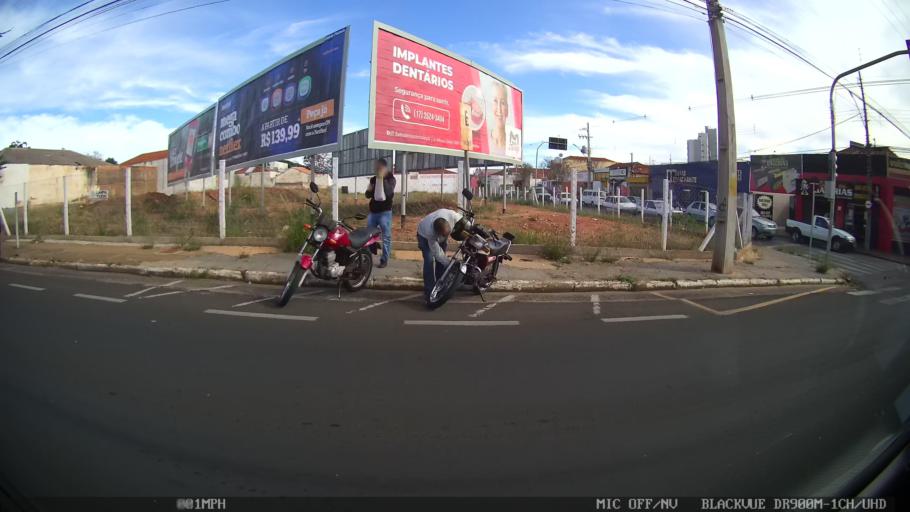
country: BR
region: Sao Paulo
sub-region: Catanduva
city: Catanduva
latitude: -21.1357
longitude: -48.9795
